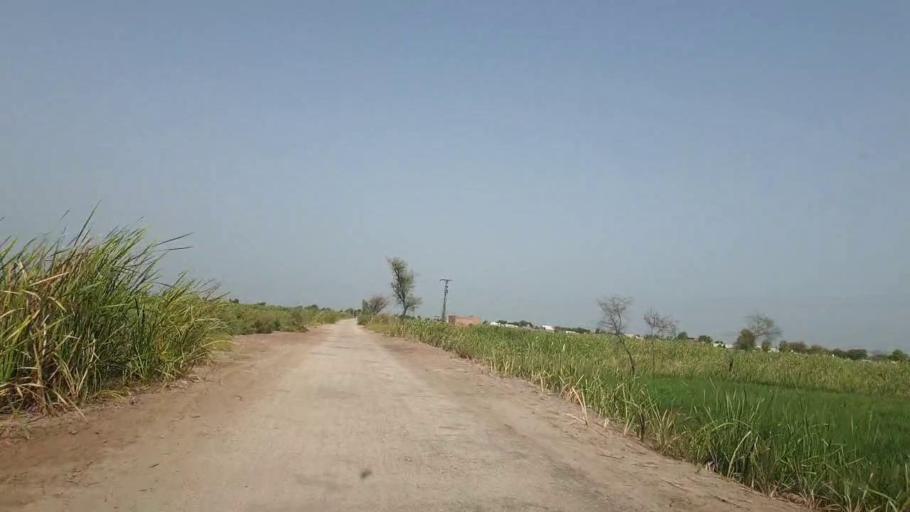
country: PK
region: Sindh
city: Sakrand
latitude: 26.3056
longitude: 68.2201
